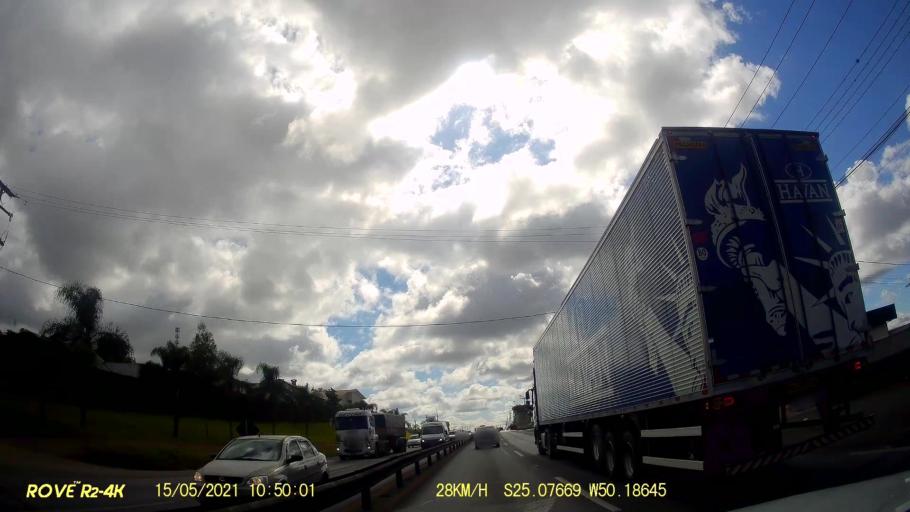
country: BR
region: Parana
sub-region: Ponta Grossa
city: Ponta Grossa
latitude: -25.0768
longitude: -50.1865
